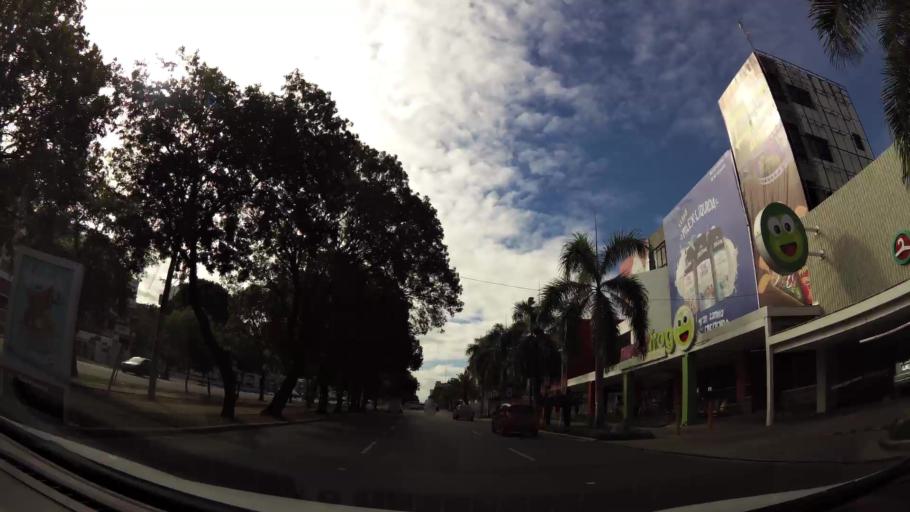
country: DO
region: Nacional
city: La Julia
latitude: 18.4752
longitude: -69.9432
